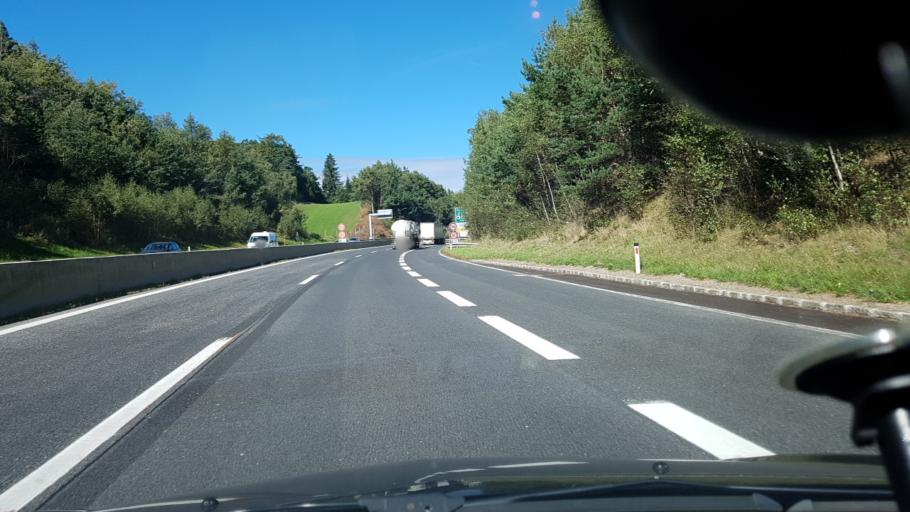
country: AT
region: Lower Austria
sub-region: Politischer Bezirk Neunkirchen
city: Zobern
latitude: 47.5308
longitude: 16.1116
